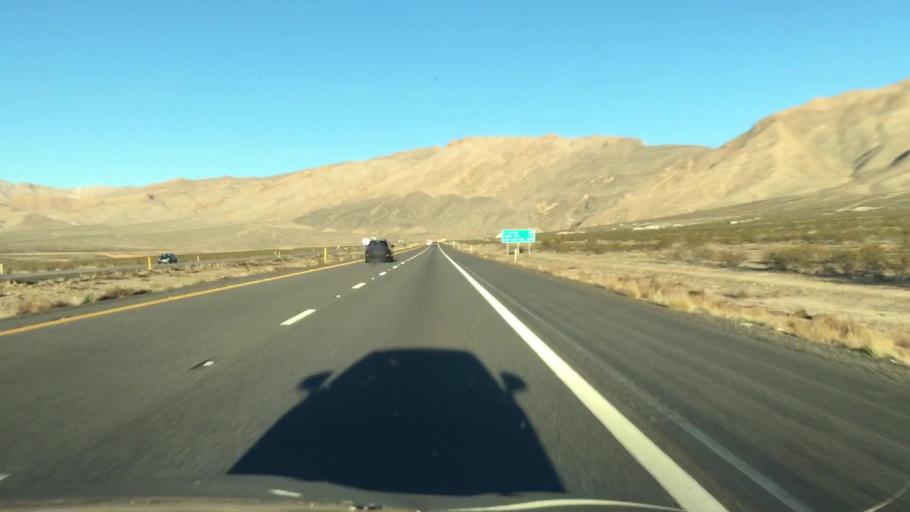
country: US
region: Arizona
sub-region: Mohave County
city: Beaver Dam
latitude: 36.9044
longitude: -113.8955
